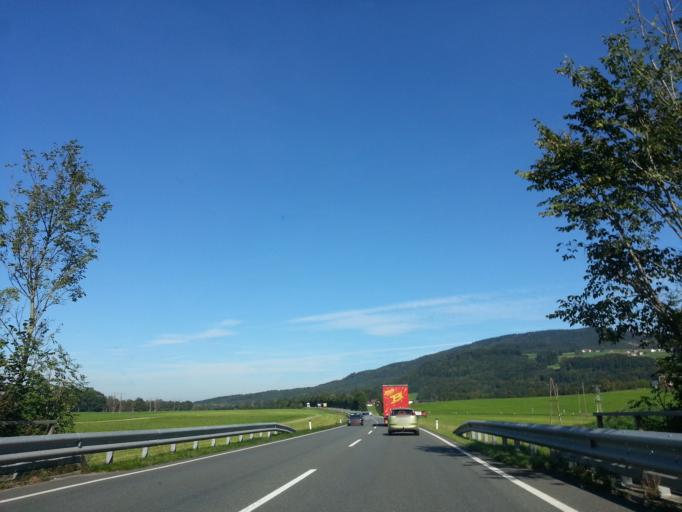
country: AT
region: Salzburg
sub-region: Politischer Bezirk Salzburg-Umgebung
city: Anthering
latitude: 47.8845
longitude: 13.0014
